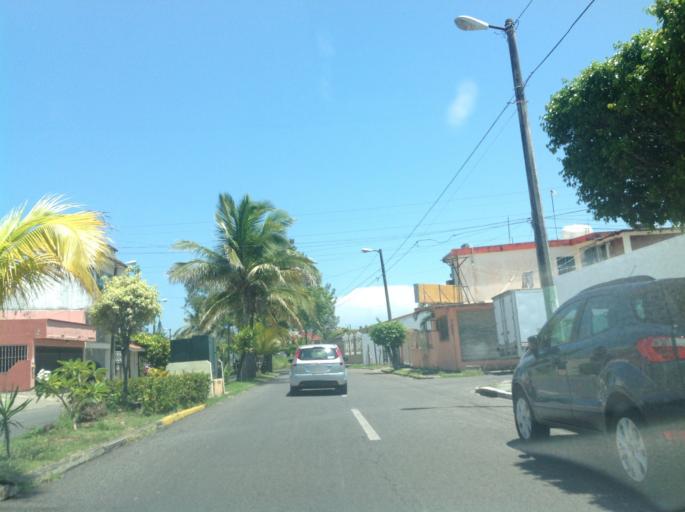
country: MX
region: Veracruz
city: Veracruz
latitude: 19.1583
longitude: -96.1372
